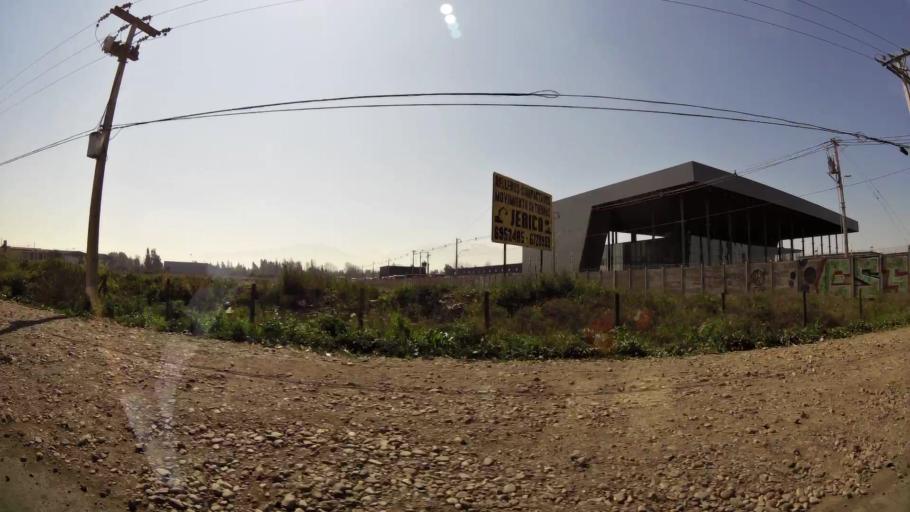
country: CL
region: Santiago Metropolitan
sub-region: Provincia de Chacabuco
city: Chicureo Abajo
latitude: -33.2795
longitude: -70.7387
